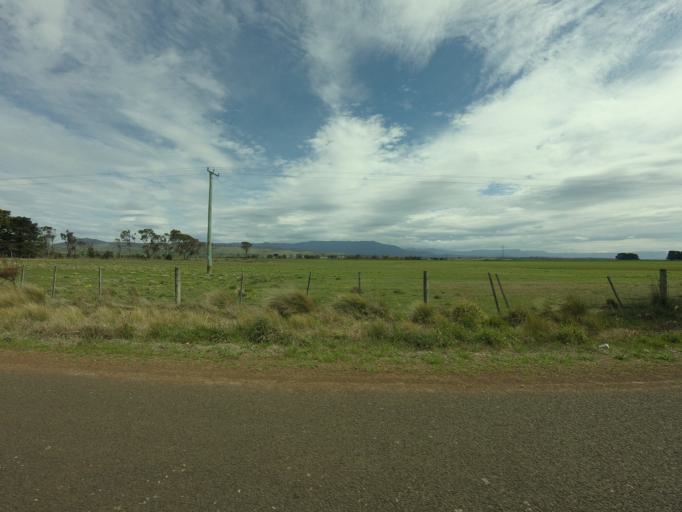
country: AU
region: Tasmania
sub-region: Northern Midlands
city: Evandale
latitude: -41.8611
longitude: 147.3462
